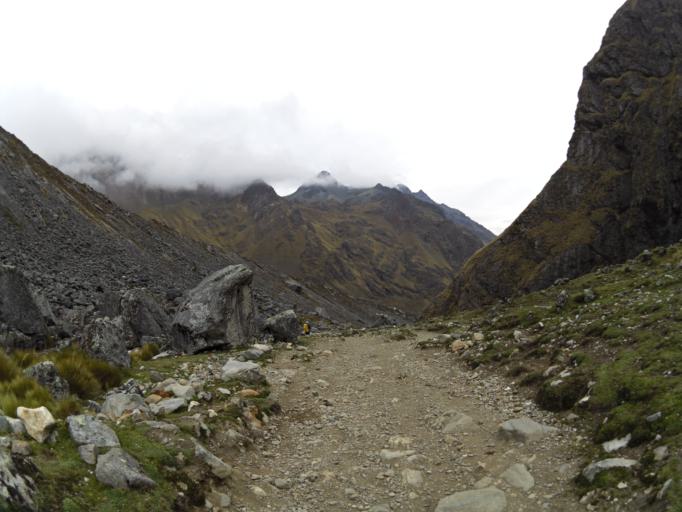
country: PE
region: Cusco
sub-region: Provincia de Anta
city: Limatambo
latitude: -13.3585
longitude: -72.5599
